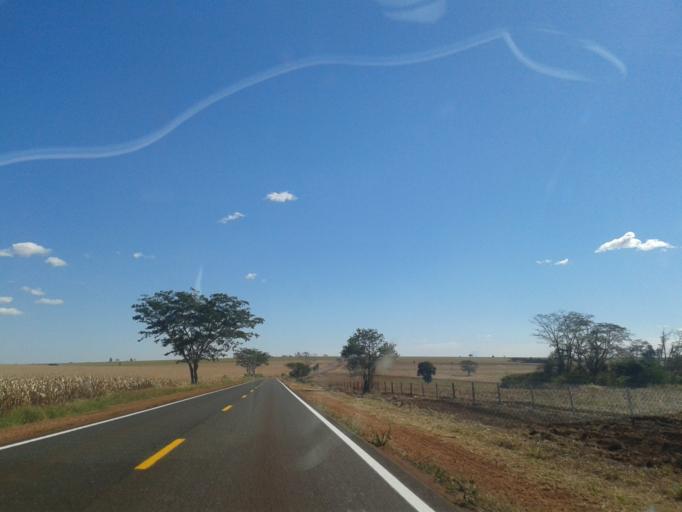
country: BR
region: Minas Gerais
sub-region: Capinopolis
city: Capinopolis
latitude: -18.6930
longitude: -49.4831
